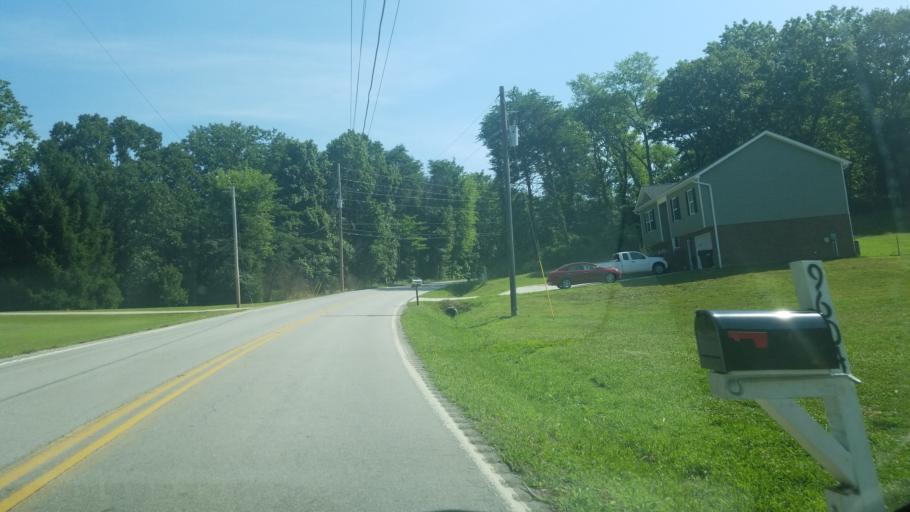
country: US
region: Tennessee
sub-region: Hamilton County
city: Lakesite
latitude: 35.2068
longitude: -85.0685
